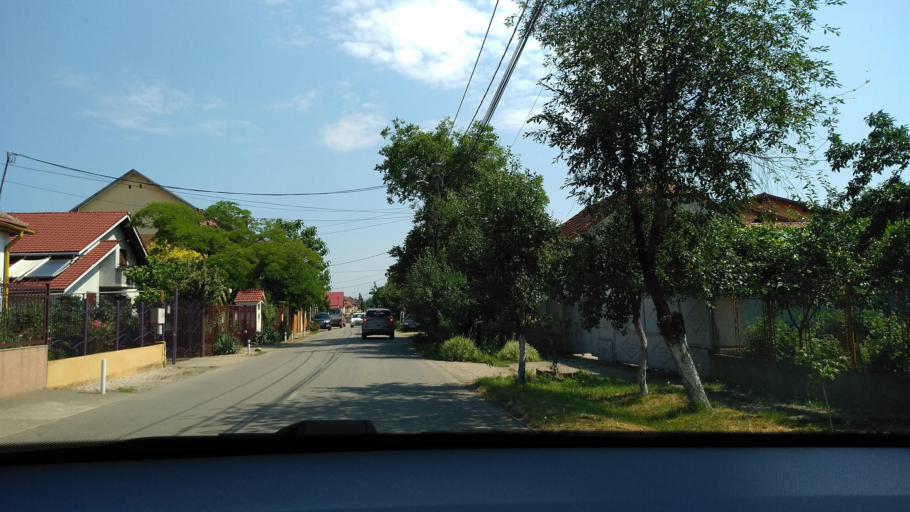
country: RO
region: Timis
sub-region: Comuna Dumbravita
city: Dumbravita
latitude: 45.7950
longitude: 21.2365
